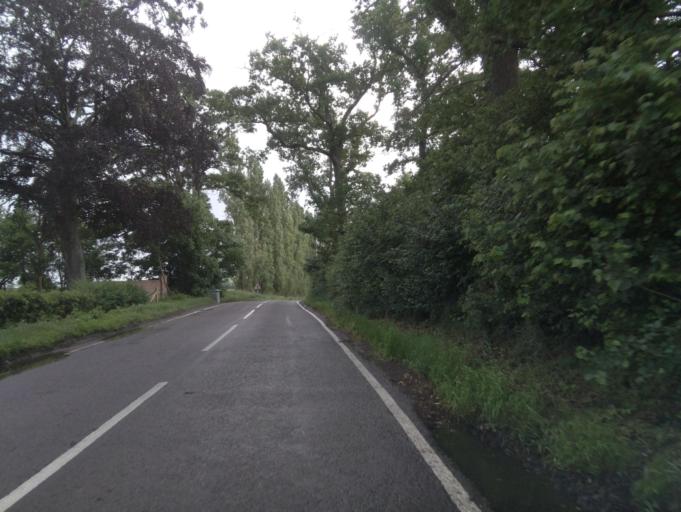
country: GB
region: England
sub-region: Lincolnshire
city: Great Gonerby
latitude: 52.9938
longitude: -0.6705
